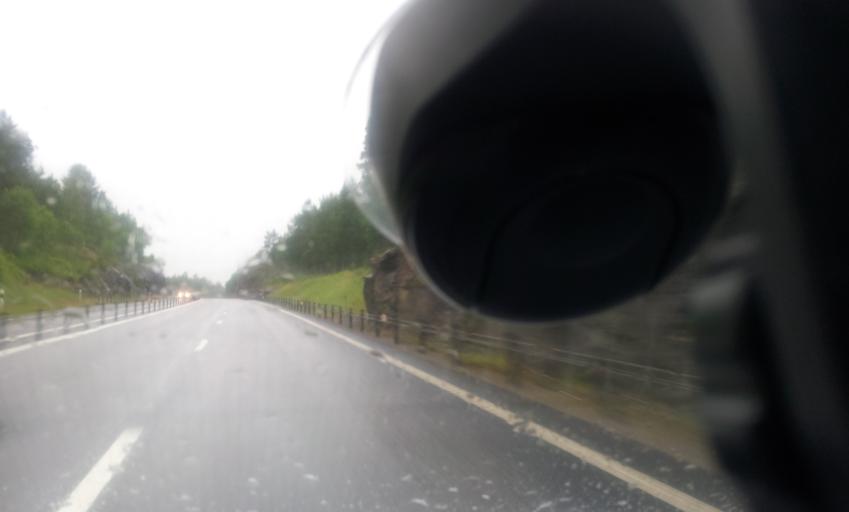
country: SE
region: OEstergoetland
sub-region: Valdemarsviks Kommun
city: Gusum
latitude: 58.3418
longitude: 16.4504
